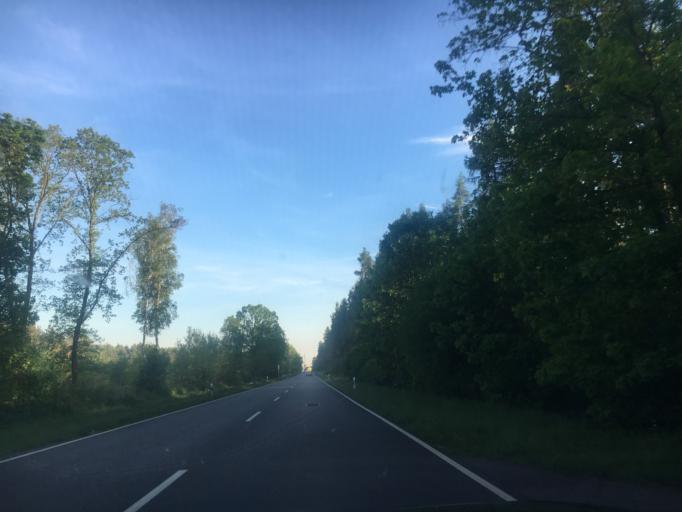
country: DE
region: Saxony-Anhalt
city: Raguhn
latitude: 51.7415
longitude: 12.2293
